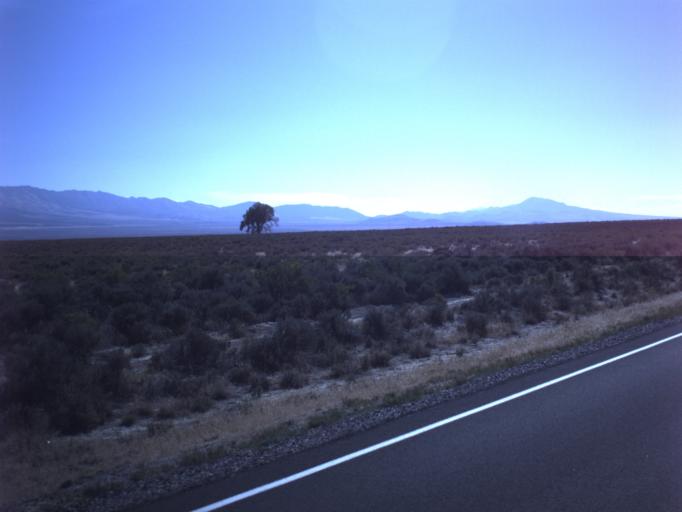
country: US
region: Utah
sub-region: Tooele County
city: Grantsville
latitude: 40.2965
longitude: -112.7426
